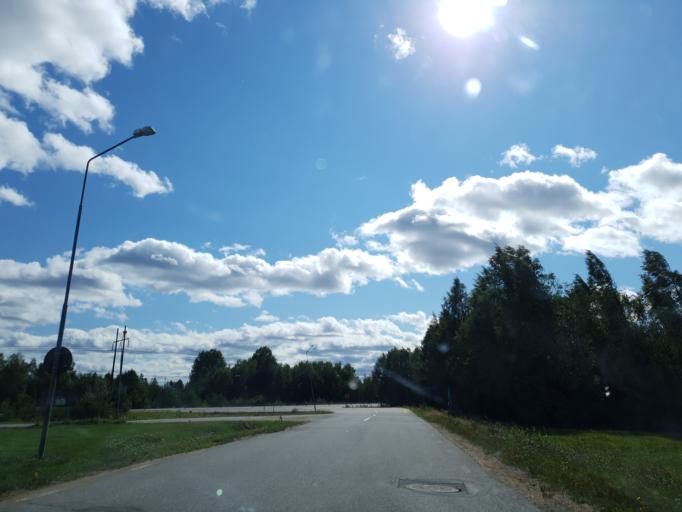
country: SE
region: Vaesterbotten
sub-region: Nordmalings Kommun
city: Nordmaling
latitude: 63.5356
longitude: 19.3992
